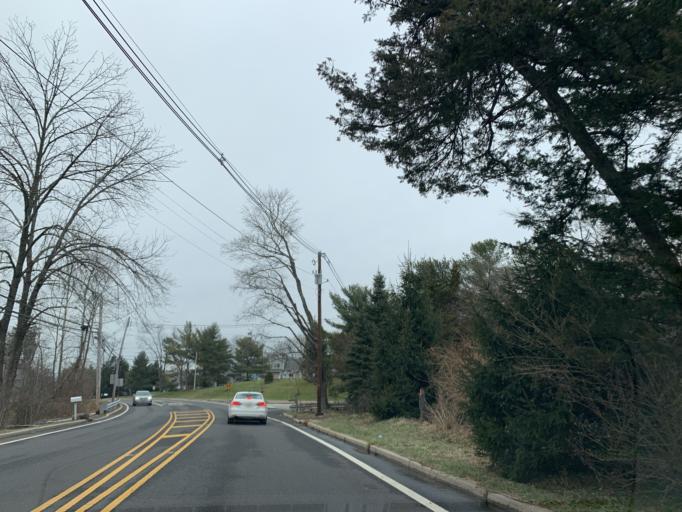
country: US
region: New Jersey
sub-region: Somerset County
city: Bedminster
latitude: 40.6467
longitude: -74.6290
